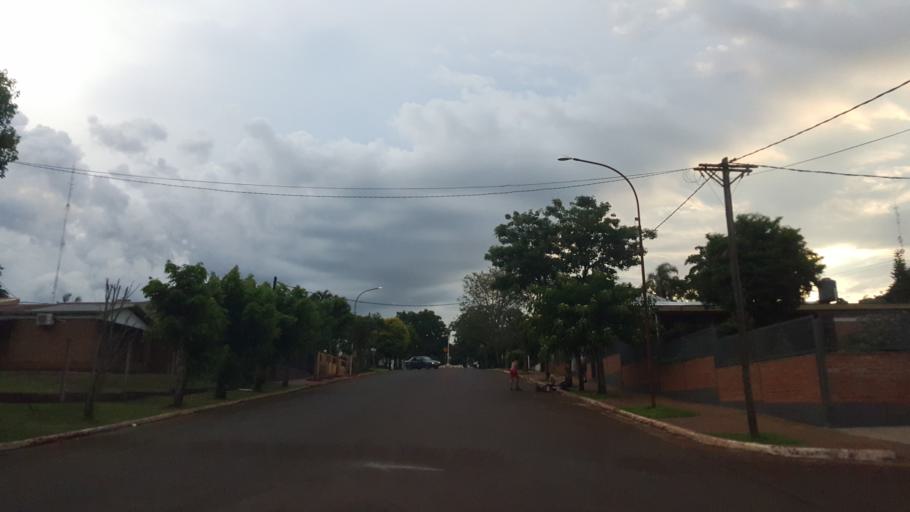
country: AR
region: Misiones
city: Jardin America
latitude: -27.0398
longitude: -55.2234
